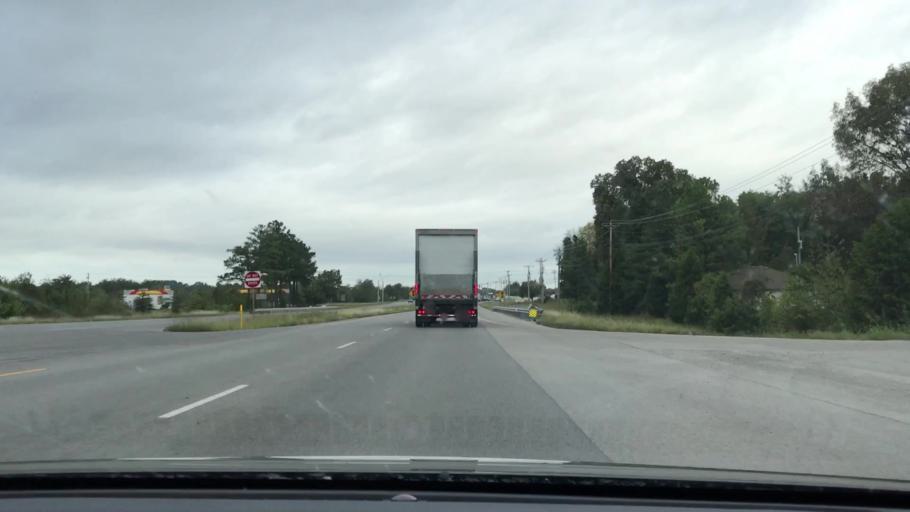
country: US
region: Kentucky
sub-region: Christian County
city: Hopkinsville
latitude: 36.8196
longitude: -87.5015
